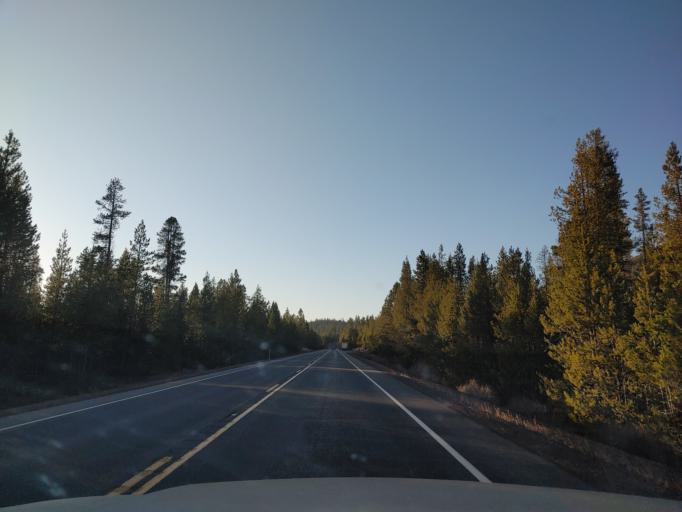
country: US
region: Oregon
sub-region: Deschutes County
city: La Pine
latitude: 43.4376
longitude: -121.8618
